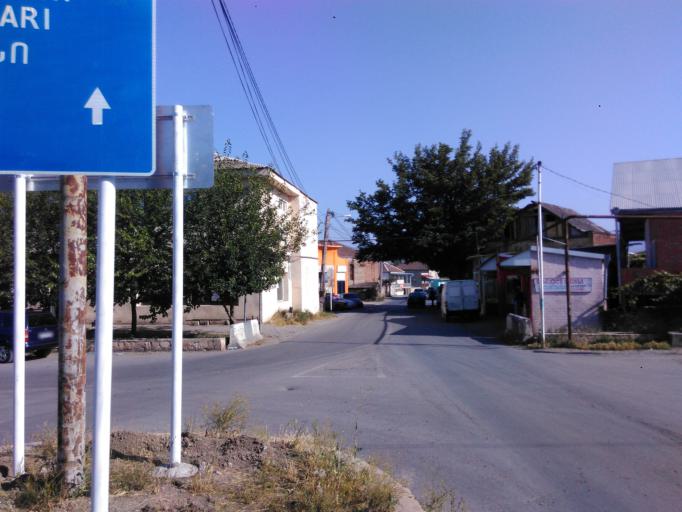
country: GE
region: Shida Kartli
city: Kaspi
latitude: 41.9326
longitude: 44.5740
